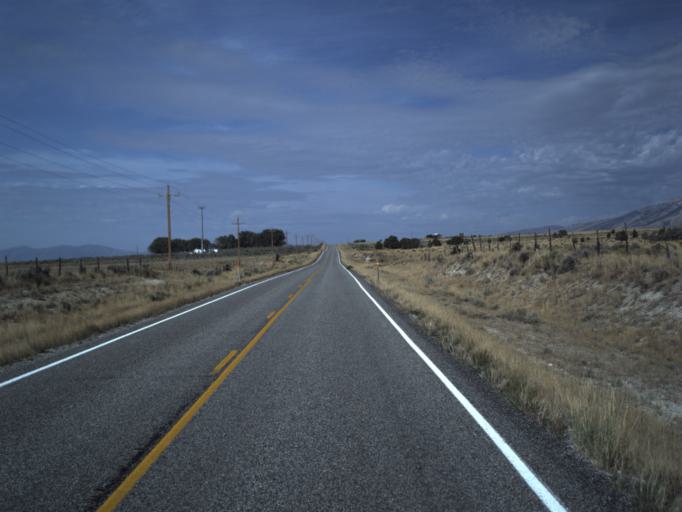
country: US
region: Idaho
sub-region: Cassia County
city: Burley
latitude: 41.8173
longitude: -113.2651
